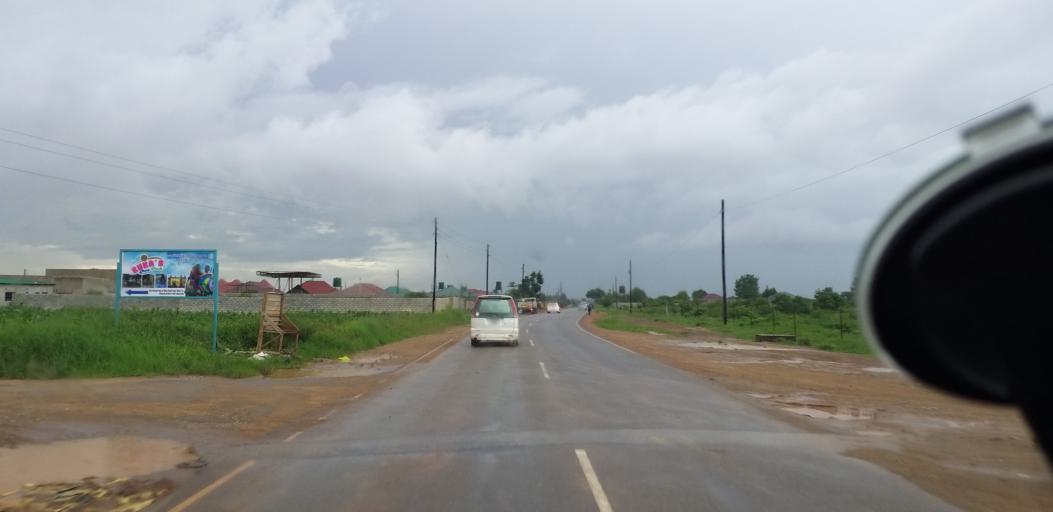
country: ZM
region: Lusaka
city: Lusaka
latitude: -15.4847
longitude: 28.3150
